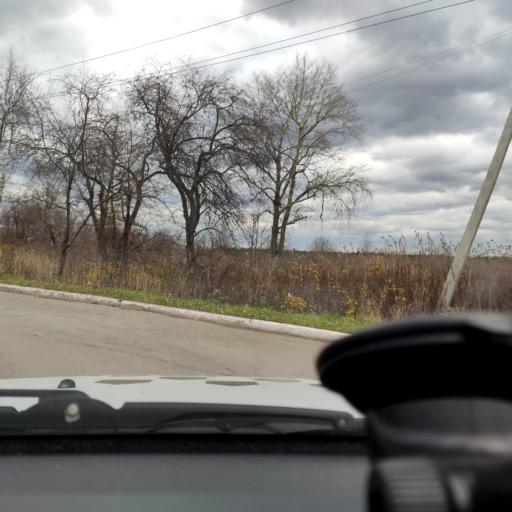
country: RU
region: Perm
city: Perm
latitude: 57.9933
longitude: 56.3375
